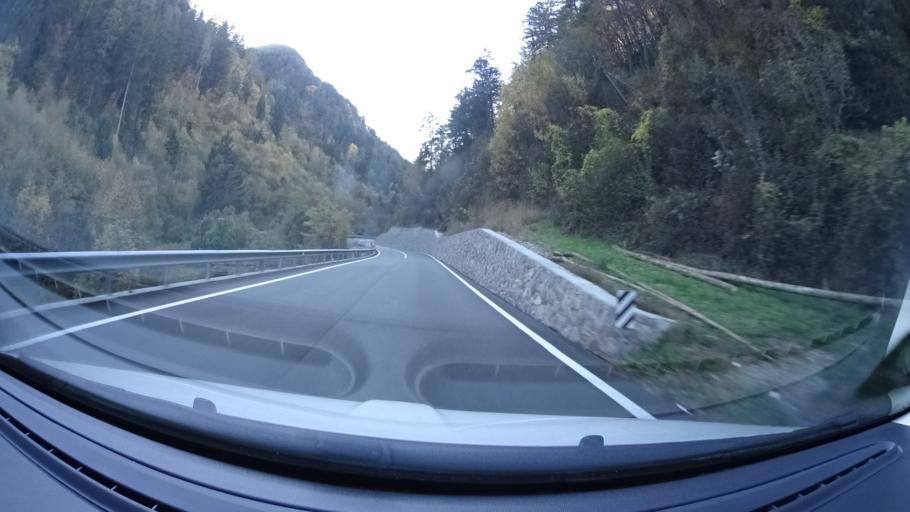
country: IT
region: Trentino-Alto Adige
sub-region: Bolzano
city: Laion
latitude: 46.5950
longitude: 11.5744
